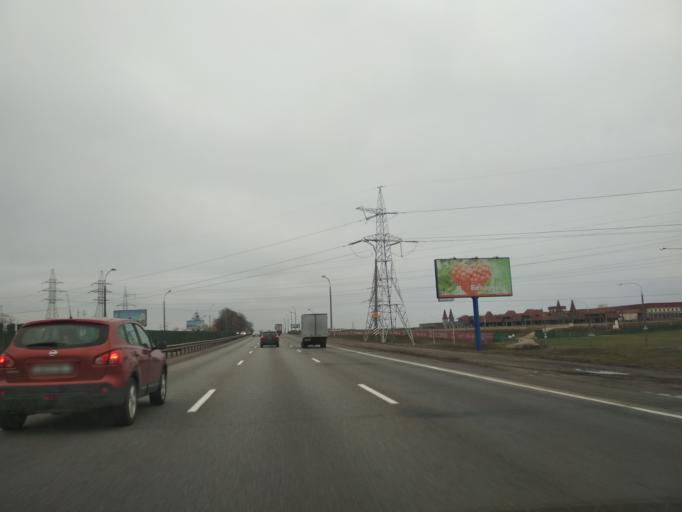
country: BY
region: Minsk
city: Yubilyeyny
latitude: 53.8393
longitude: 27.4993
